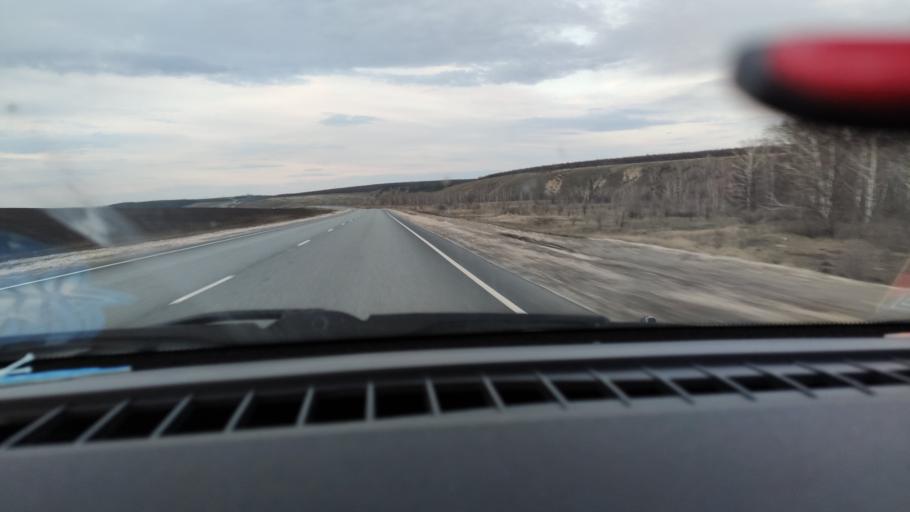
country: RU
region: Saratov
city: Yelshanka
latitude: 51.8595
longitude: 46.4976
